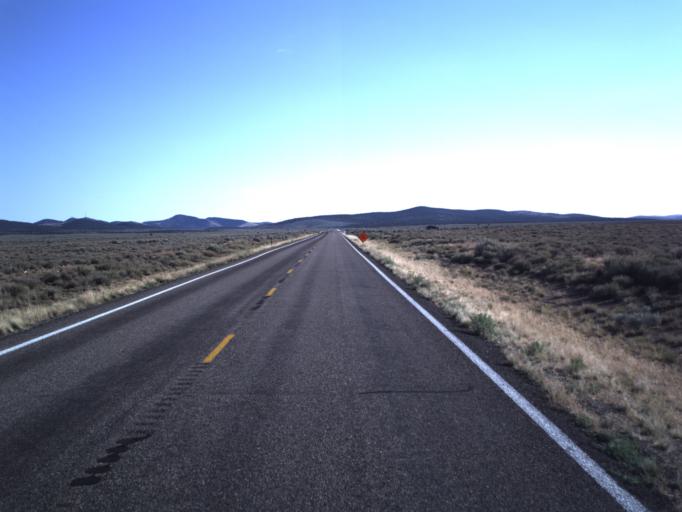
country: US
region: Utah
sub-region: Iron County
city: Enoch
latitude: 37.9817
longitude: -113.0031
